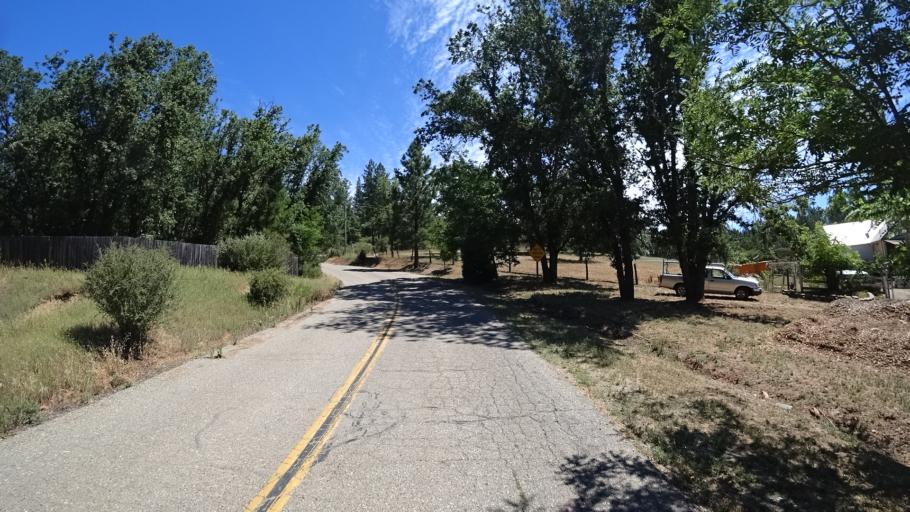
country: US
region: California
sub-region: Amador County
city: Pioneer
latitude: 38.3543
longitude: -120.5200
